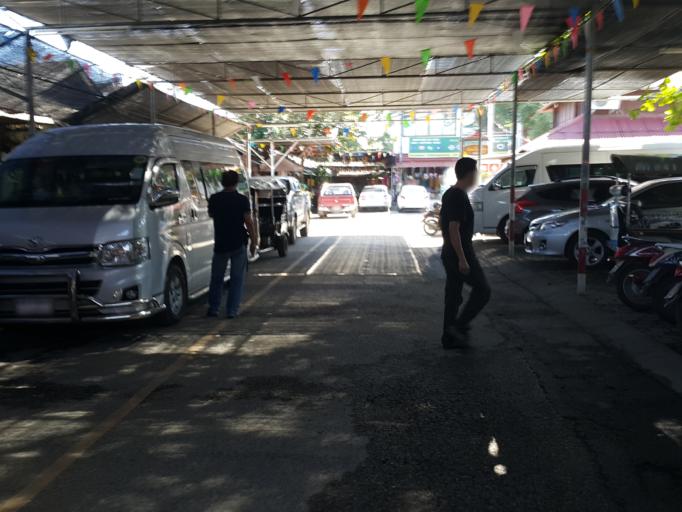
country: TH
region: Chiang Mai
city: Hang Dong
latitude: 18.6881
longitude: 98.9470
